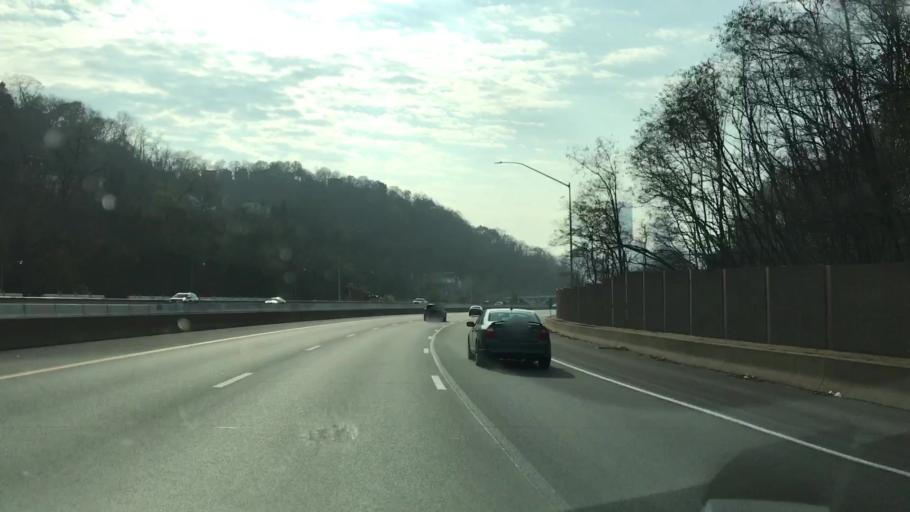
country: US
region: Pennsylvania
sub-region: Allegheny County
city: Pittsburgh
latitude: 40.4660
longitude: -80.0004
